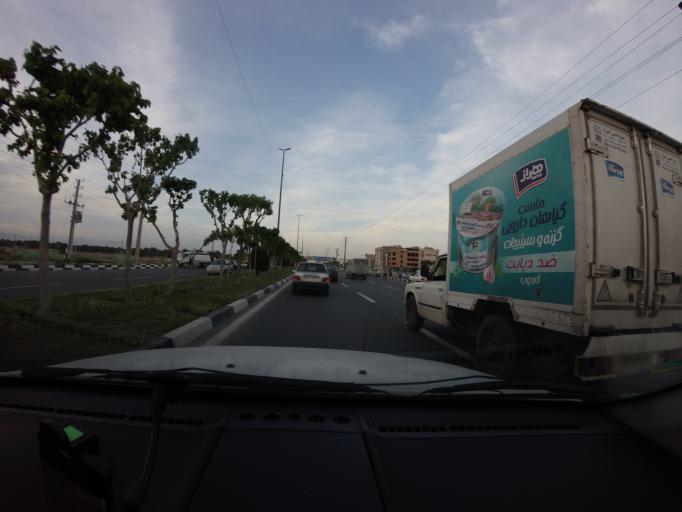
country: IR
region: Tehran
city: Eslamshahr
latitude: 35.5404
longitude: 51.2115
